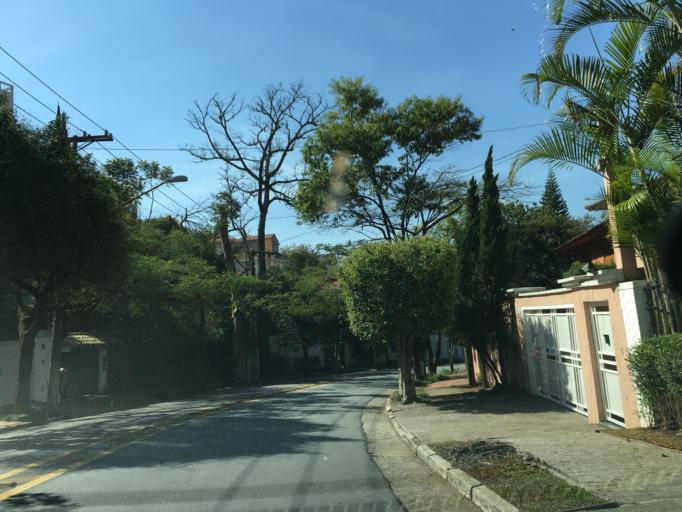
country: BR
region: Sao Paulo
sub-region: Sao Paulo
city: Sao Paulo
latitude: -23.5397
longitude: -46.6675
